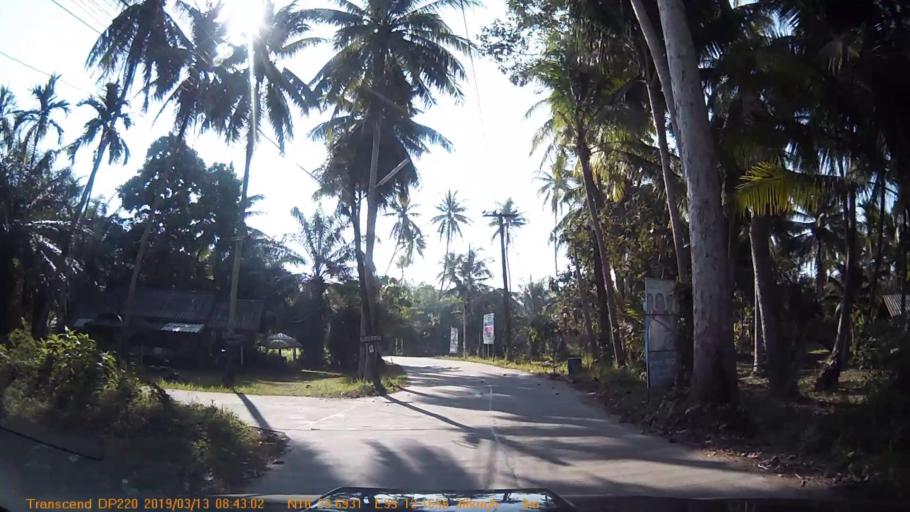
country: TH
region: Chumphon
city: Chumphon
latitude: 10.4949
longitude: 99.2195
